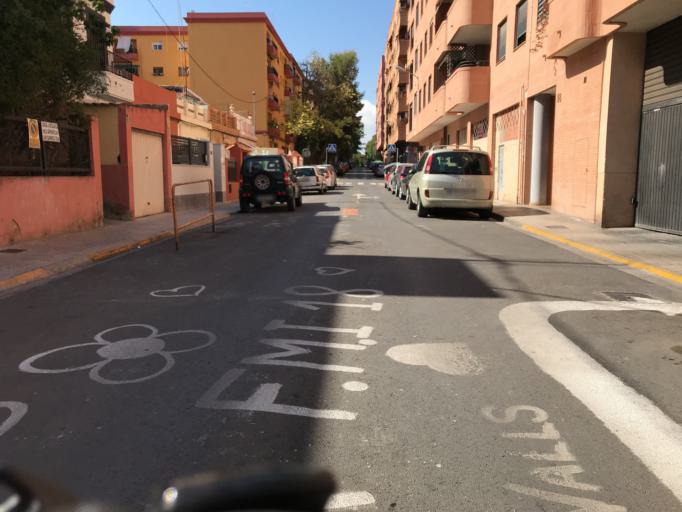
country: ES
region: Valencia
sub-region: Provincia de Valencia
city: Burjassot
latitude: 39.5145
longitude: -0.4145
